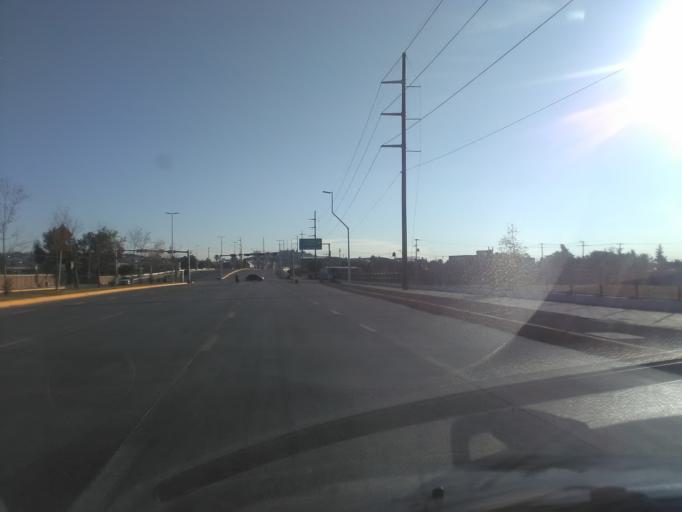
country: MX
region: Durango
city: Victoria de Durango
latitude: 24.0028
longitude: -104.6976
